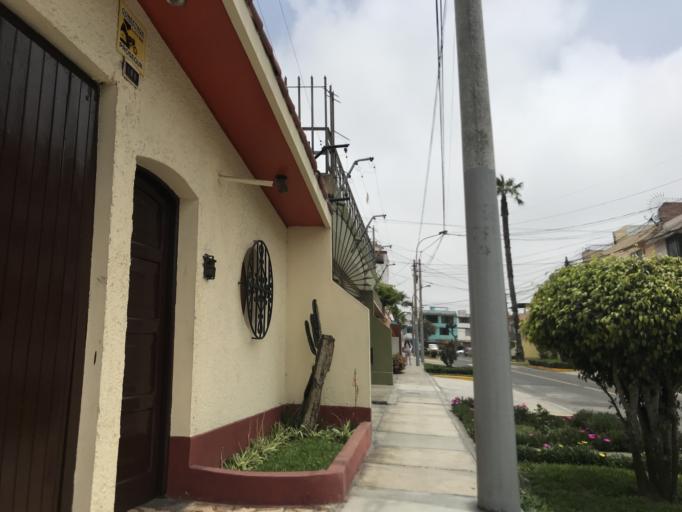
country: PE
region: Lima
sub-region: Lima
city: San Isidro
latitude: -12.0831
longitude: -77.0764
